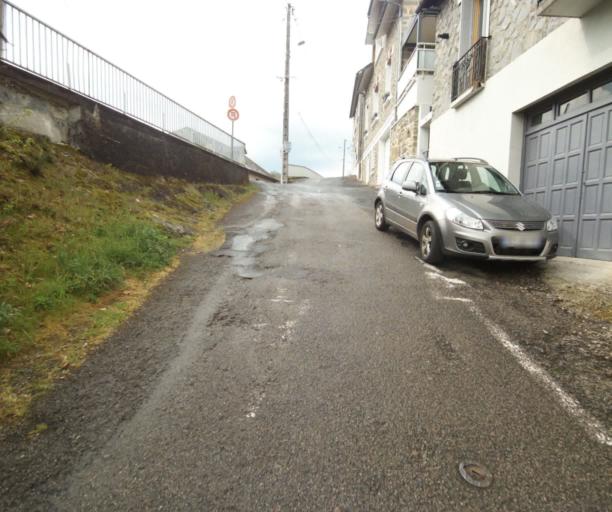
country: FR
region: Limousin
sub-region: Departement de la Correze
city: Tulle
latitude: 45.2606
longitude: 1.7530
